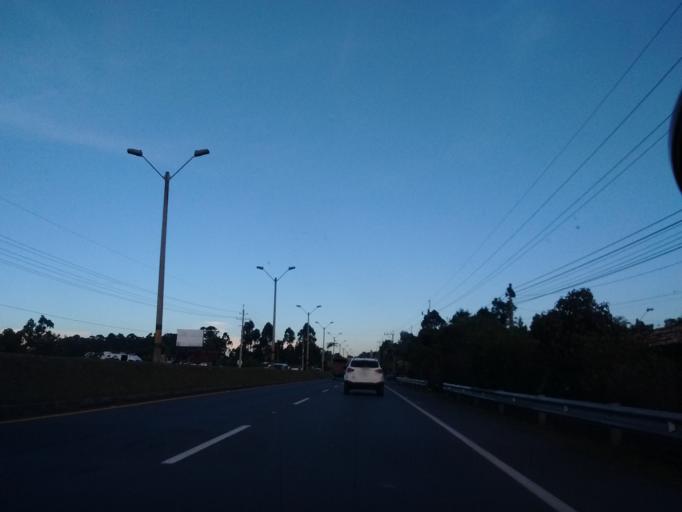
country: CO
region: Antioquia
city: Rionegro
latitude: 6.1837
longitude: -75.3742
